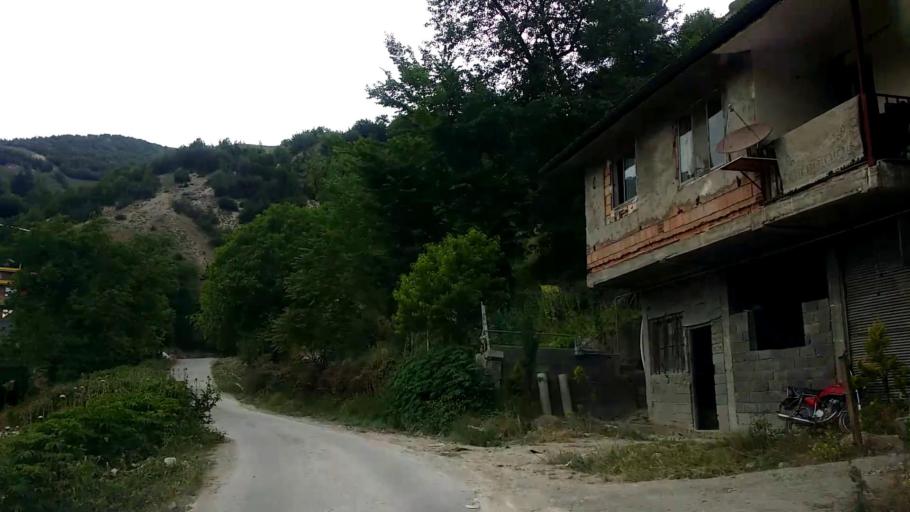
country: IR
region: Mazandaran
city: Chalus
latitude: 36.5554
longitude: 51.2757
